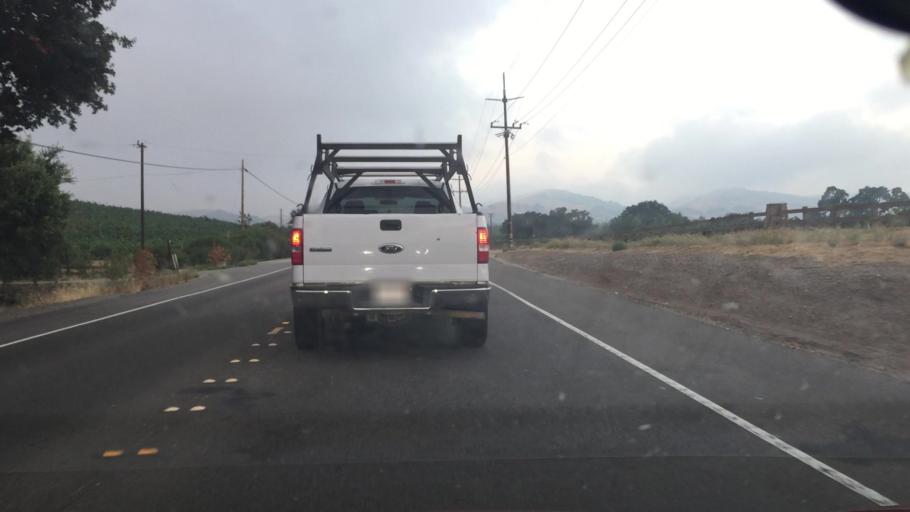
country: US
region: California
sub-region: Alameda County
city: Livermore
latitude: 37.6422
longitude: -121.7928
